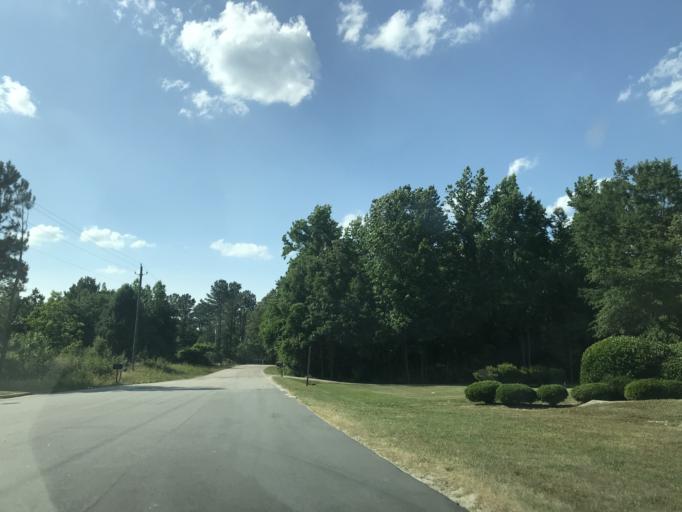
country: US
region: North Carolina
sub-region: Wake County
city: Garner
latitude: 35.7238
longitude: -78.5610
